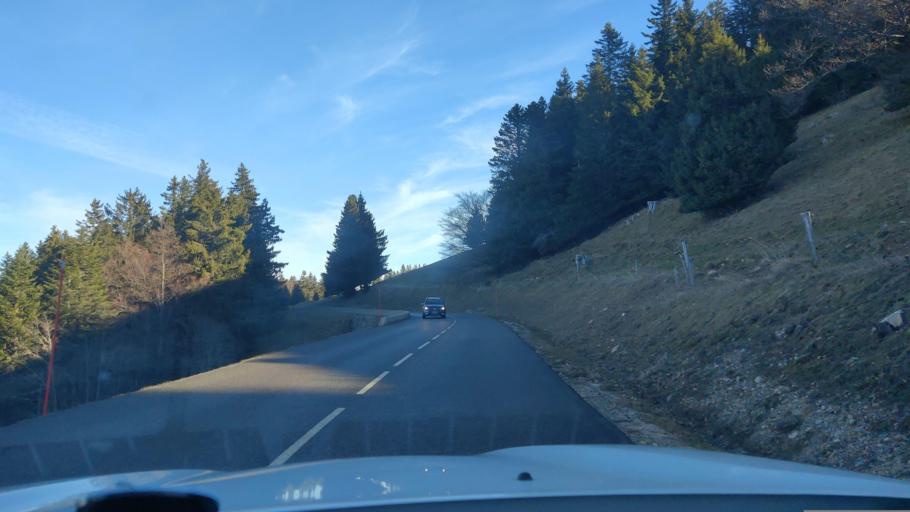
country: FR
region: Rhone-Alpes
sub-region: Departement de la Savoie
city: Mouxy
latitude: 45.6744
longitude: 5.9754
